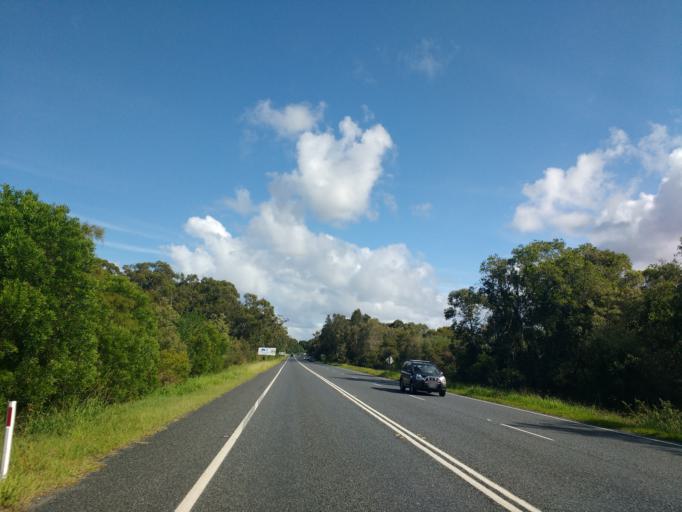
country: AU
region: New South Wales
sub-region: Ballina
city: Ballina
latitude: -28.9421
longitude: 153.4689
